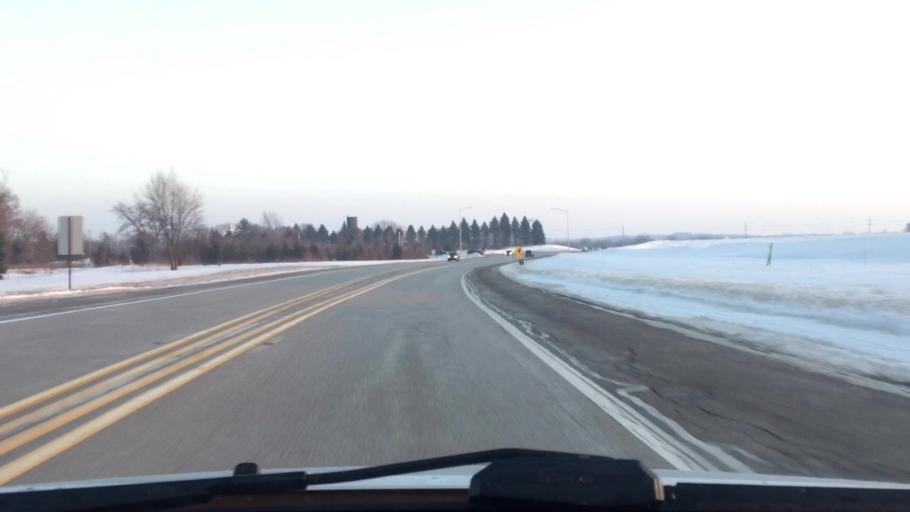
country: US
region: Illinois
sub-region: Kane County
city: Village of Campton Hills
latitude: 41.9437
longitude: -88.3993
